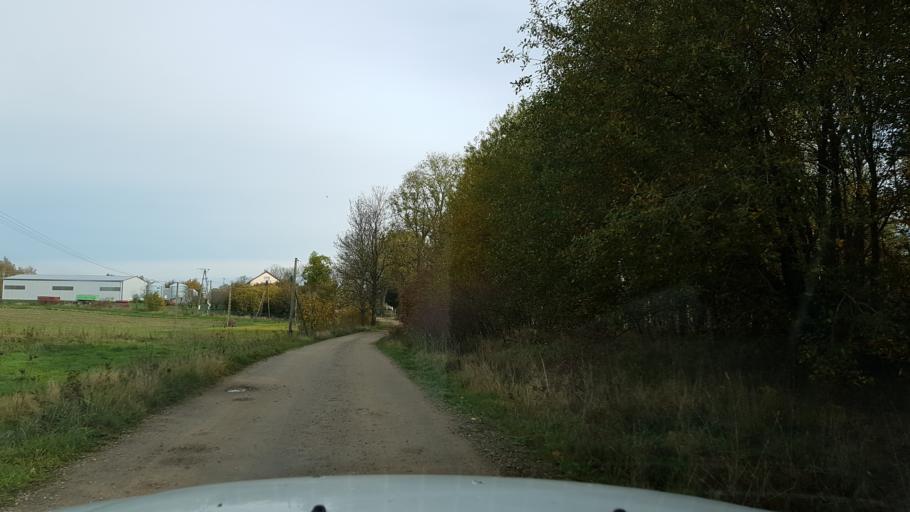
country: PL
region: West Pomeranian Voivodeship
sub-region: Powiat swidwinski
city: Polczyn-Zdroj
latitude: 53.7354
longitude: 16.0343
